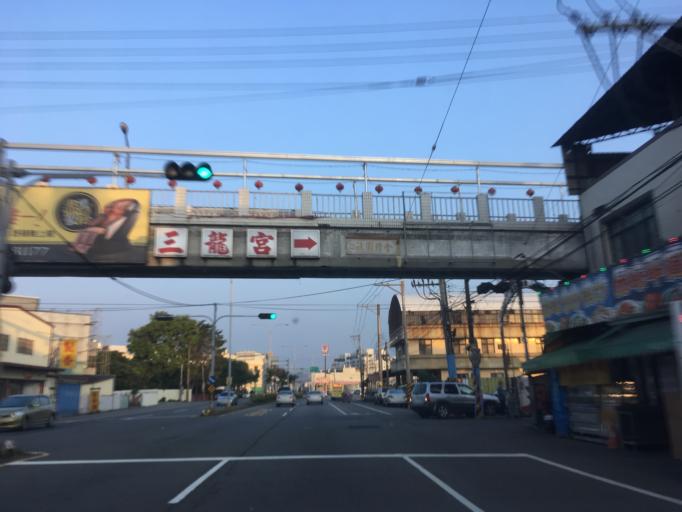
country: TW
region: Taiwan
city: Zhongxing New Village
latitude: 23.9964
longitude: 120.6638
